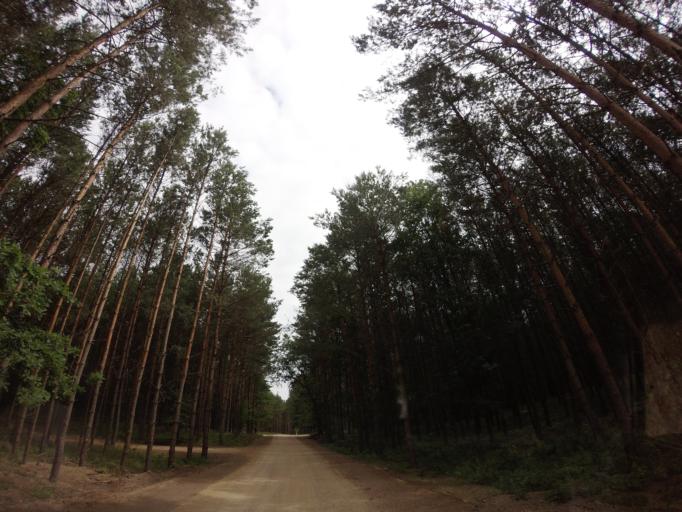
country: PL
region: Lubusz
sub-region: Powiat strzelecko-drezdenecki
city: Stare Kurowo
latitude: 52.8845
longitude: 15.6348
